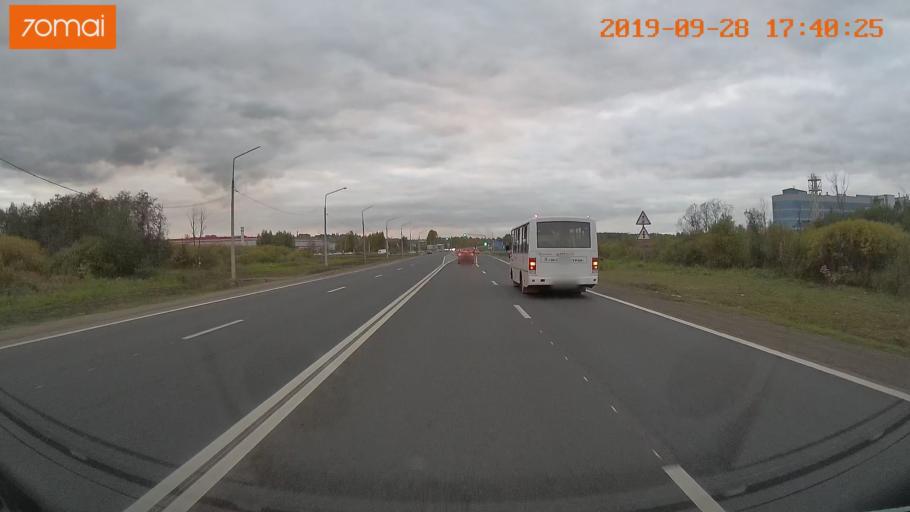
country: RU
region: Jaroslavl
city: Yaroslavl
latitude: 57.5499
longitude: 39.8948
